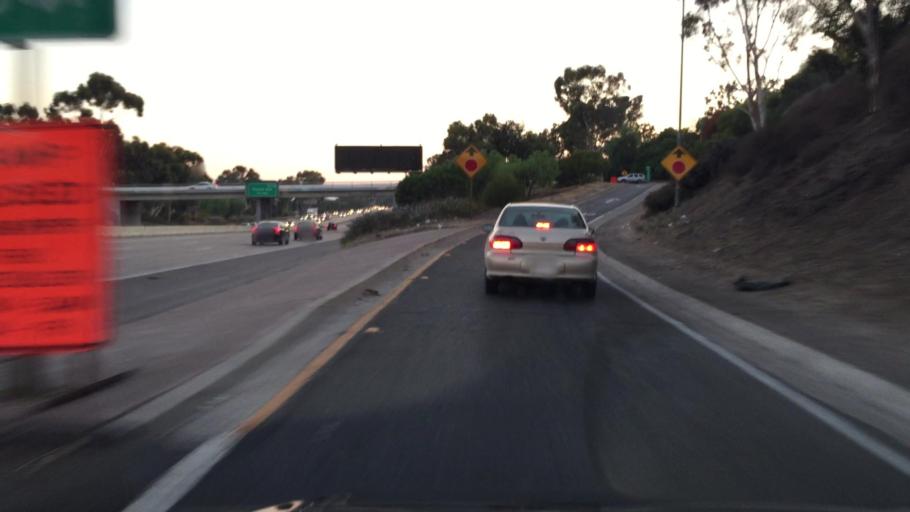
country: US
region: California
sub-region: San Diego County
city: Lemon Grove
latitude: 32.7247
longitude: -117.0753
